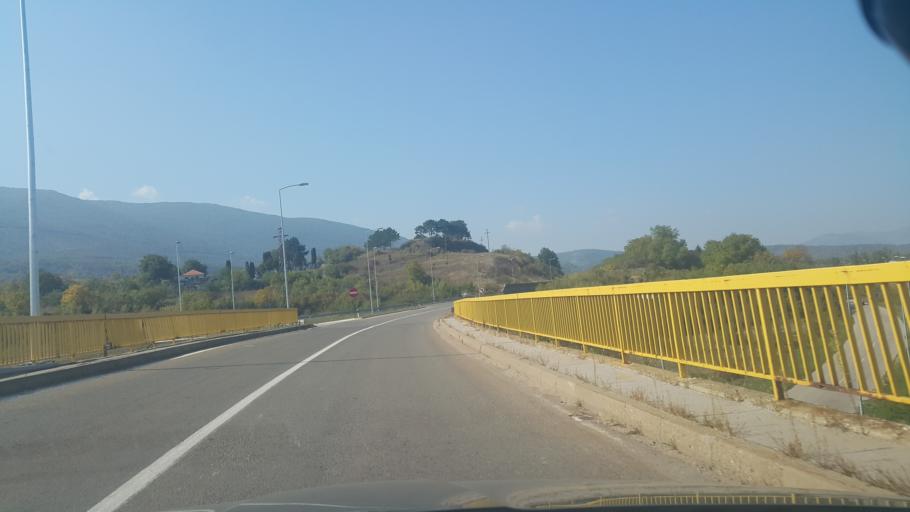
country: RS
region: Central Serbia
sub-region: Pirotski Okrug
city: Bela Palanka
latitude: 43.2228
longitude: 22.2997
